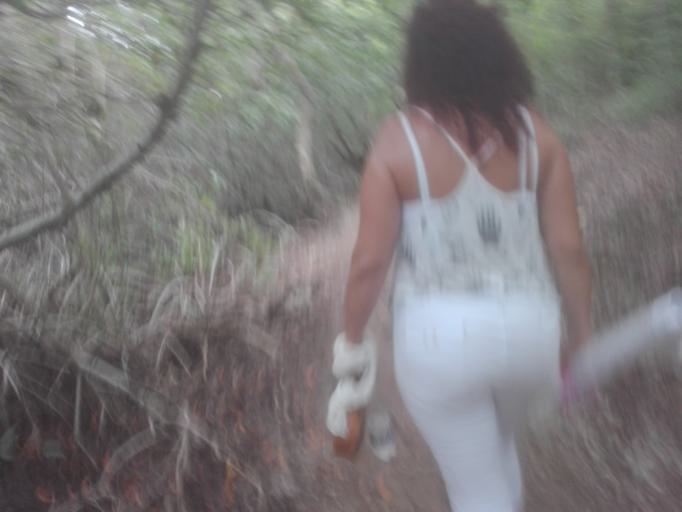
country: CO
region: Bolivar
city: Turbana
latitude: 10.1747
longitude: -75.7424
